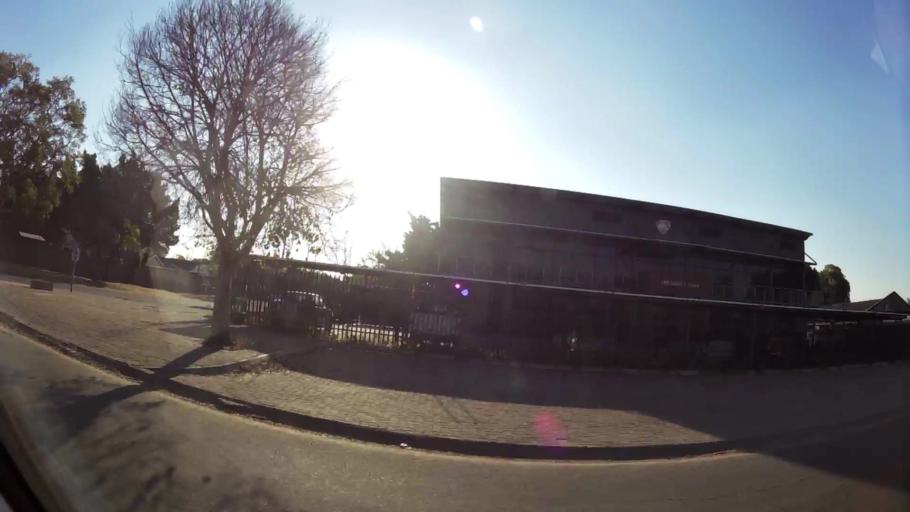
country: ZA
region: North-West
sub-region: Bojanala Platinum District Municipality
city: Rustenburg
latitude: -25.6760
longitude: 27.2360
